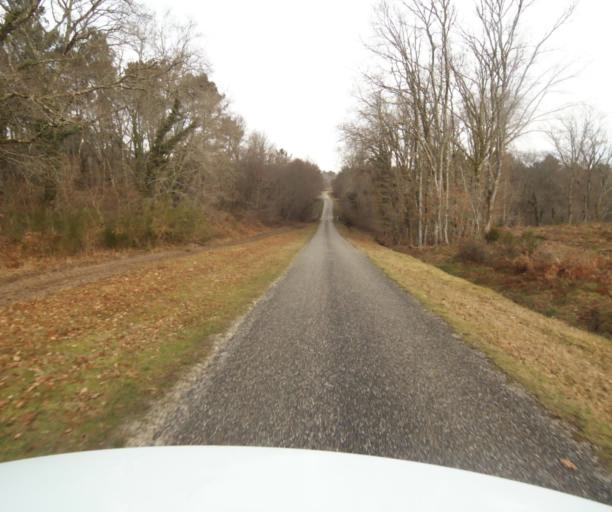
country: FR
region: Aquitaine
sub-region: Departement des Landes
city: Gabarret
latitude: 44.0793
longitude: 0.0786
